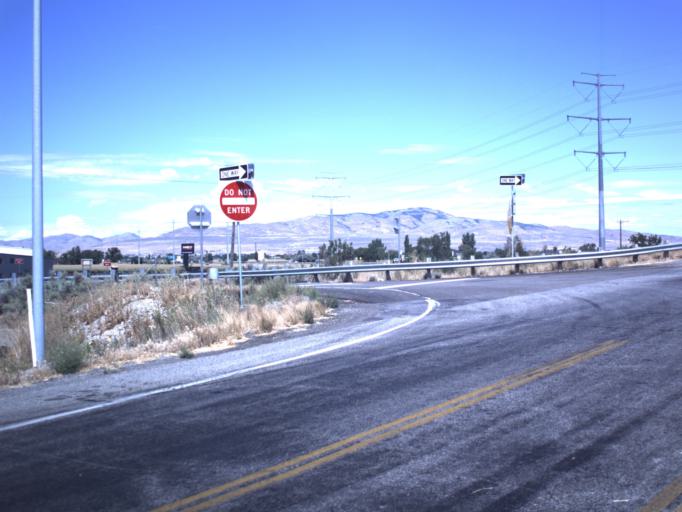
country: US
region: Utah
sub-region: Box Elder County
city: Elwood
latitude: 41.6779
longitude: -112.1411
